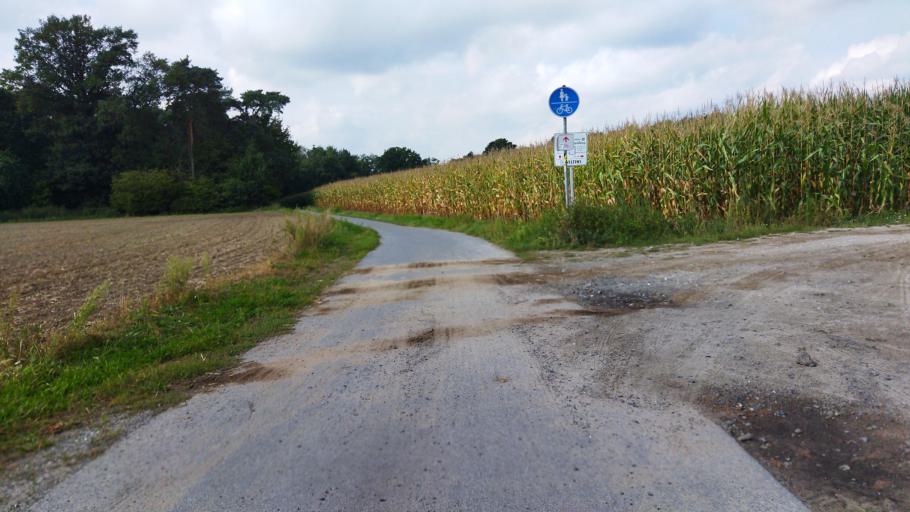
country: DE
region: North Rhine-Westphalia
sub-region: Regierungsbezirk Munster
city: Everswinkel
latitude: 51.9638
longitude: 7.9076
